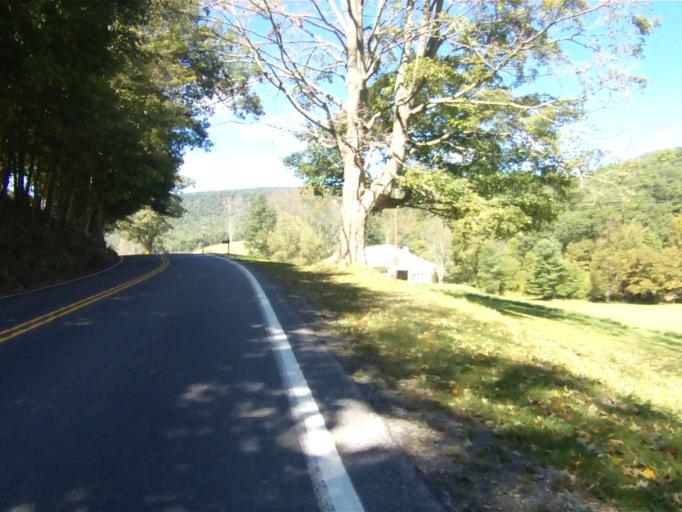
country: US
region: Pennsylvania
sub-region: Centre County
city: Milesburg
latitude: 40.9300
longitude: -77.9077
